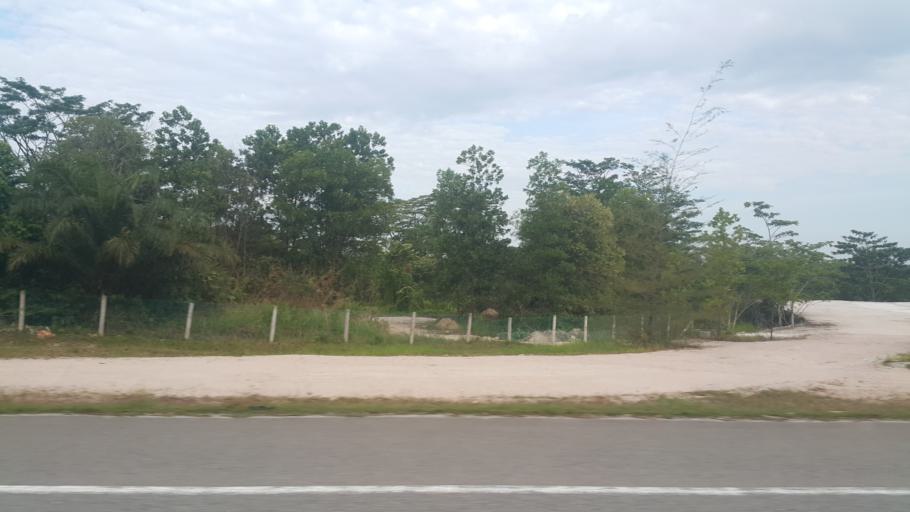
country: MY
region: Johor
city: Pekan Nenas
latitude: 1.4185
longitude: 103.5985
